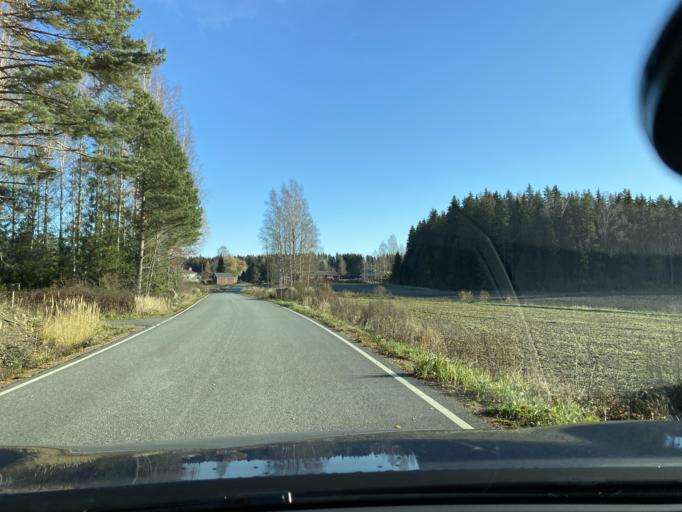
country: FI
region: Haeme
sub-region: Haemeenlinna
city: Kalvola
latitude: 61.0267
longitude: 24.1738
